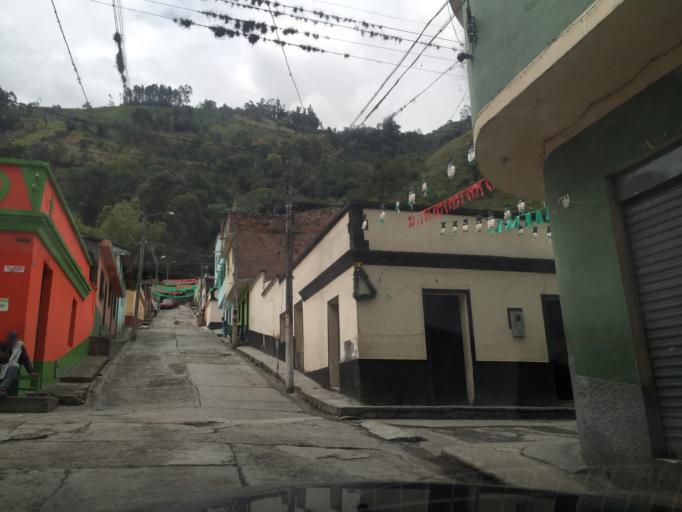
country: CO
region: Tolima
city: Cajamarca
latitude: 4.3969
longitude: -75.4451
